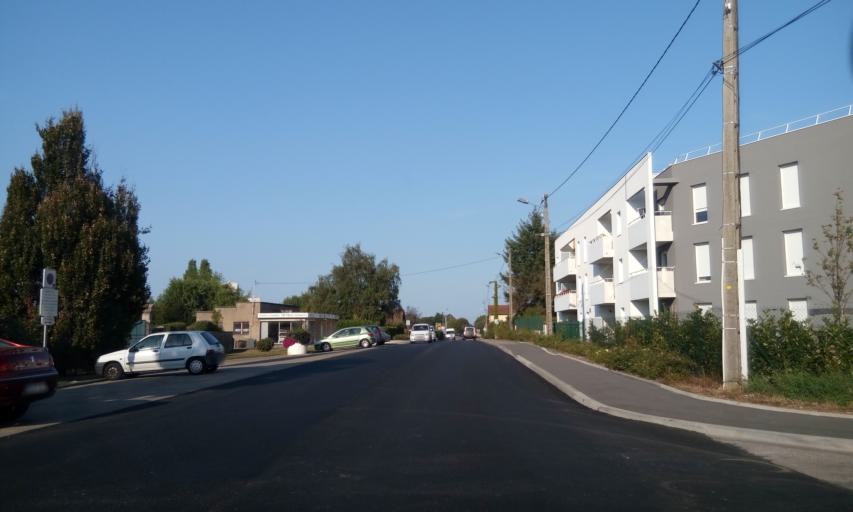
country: FR
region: Rhone-Alpes
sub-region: Departement de l'Ain
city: Villars-les-Dombes
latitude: 46.0051
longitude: 5.0310
